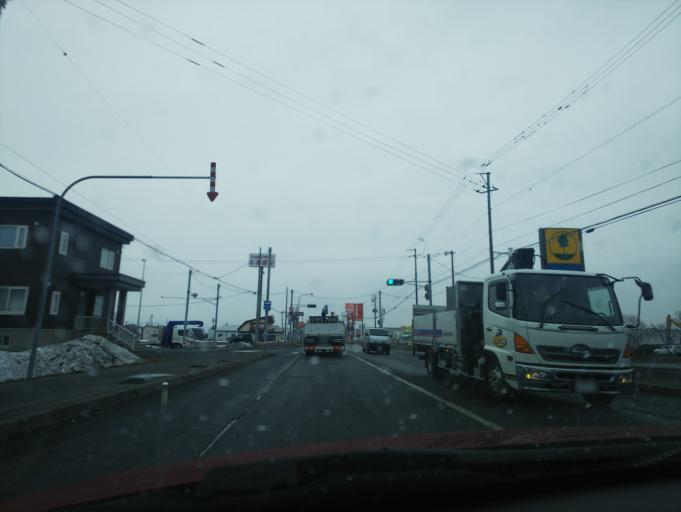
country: JP
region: Hokkaido
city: Nayoro
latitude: 44.1608
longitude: 142.3969
